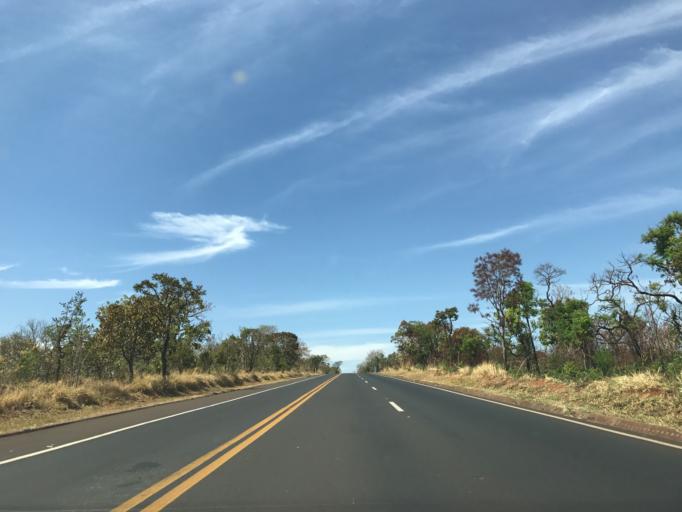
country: BR
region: Minas Gerais
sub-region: Monte Alegre De Minas
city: Monte Alegre de Minas
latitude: -18.9698
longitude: -49.0251
